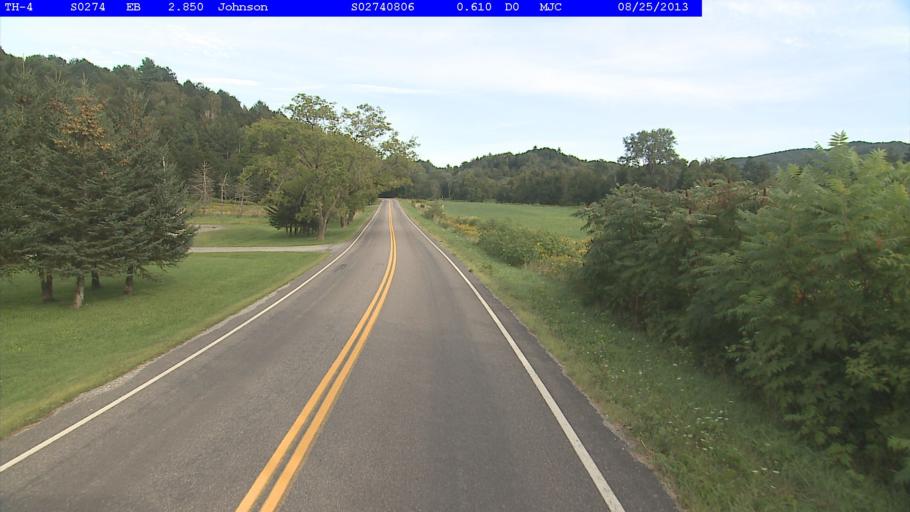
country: US
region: Vermont
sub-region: Lamoille County
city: Johnson
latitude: 44.6533
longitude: -72.7397
